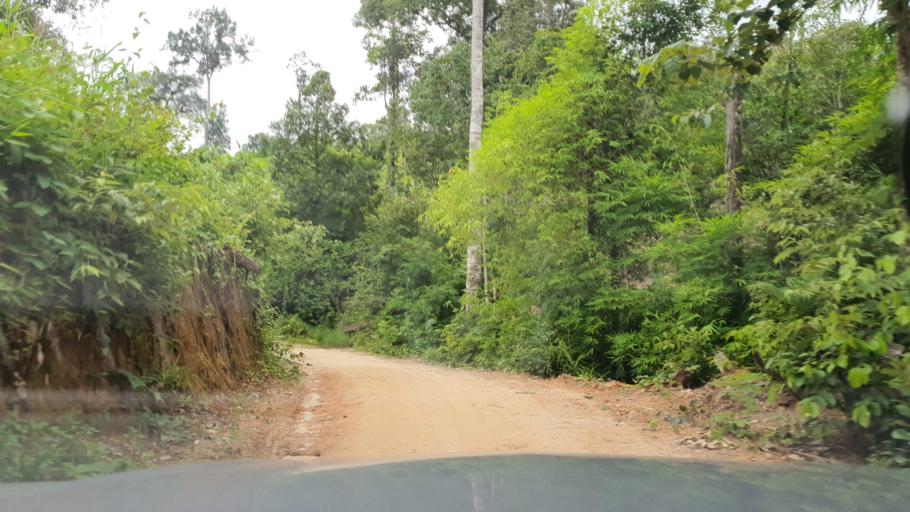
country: TH
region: Chiang Mai
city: Mae Wang
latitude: 18.6625
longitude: 98.6202
